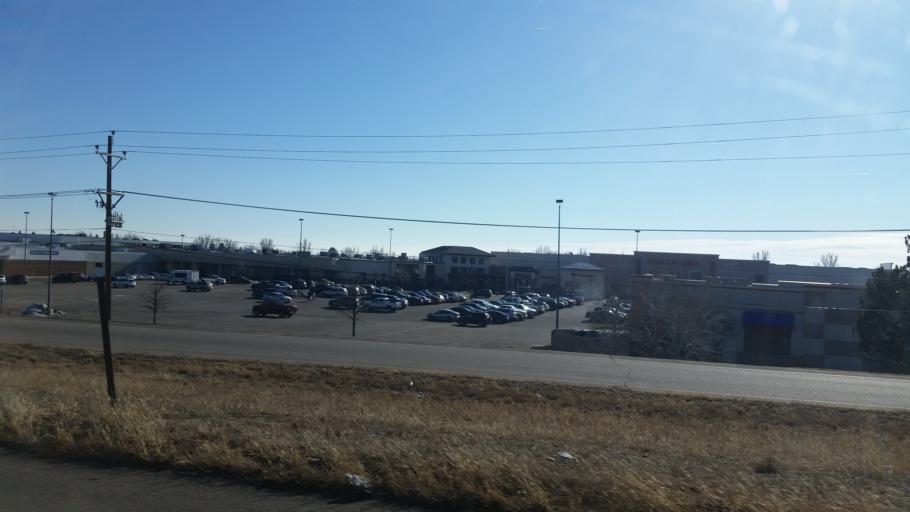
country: US
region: Colorado
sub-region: Weld County
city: Evans
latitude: 40.3920
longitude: -104.7143
